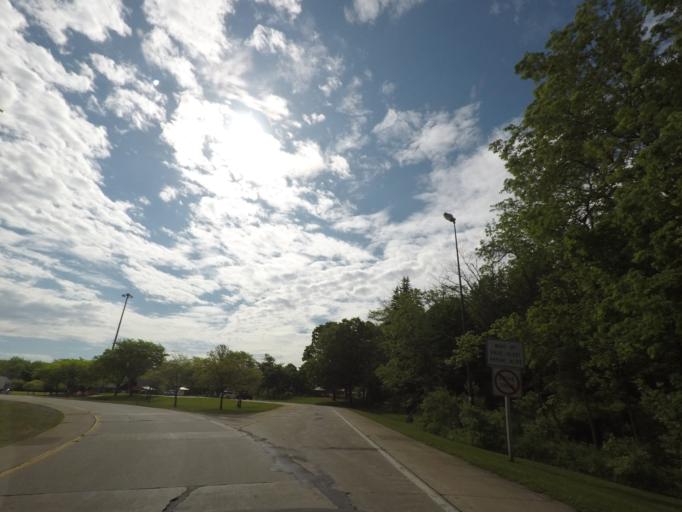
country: US
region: Illinois
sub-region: McLean County
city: Twin Grove
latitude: 40.3599
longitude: -89.1112
